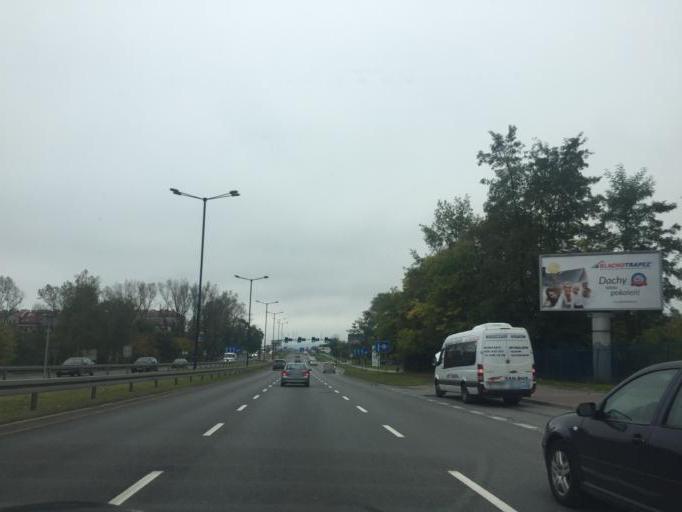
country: PL
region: Lesser Poland Voivodeship
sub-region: Powiat wielicki
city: Czarnochowice
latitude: 50.0099
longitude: 20.0091
